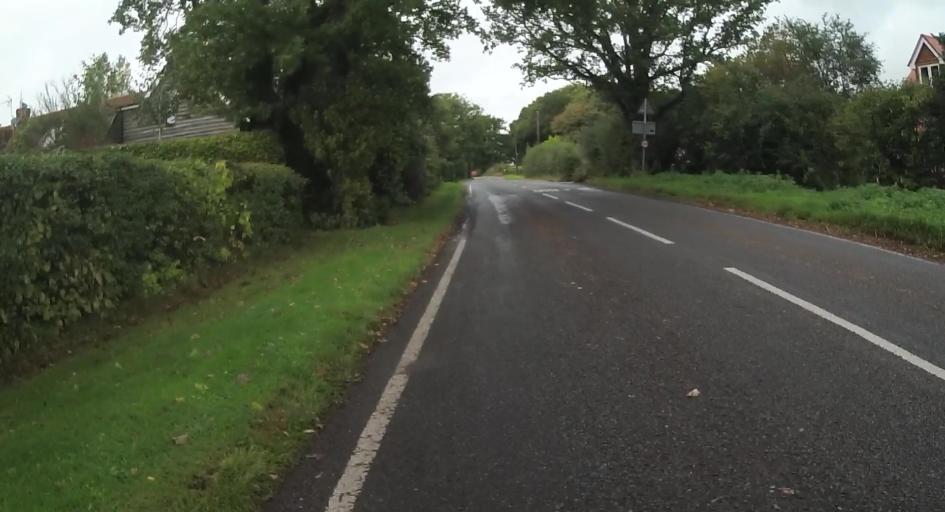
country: GB
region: England
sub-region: Hampshire
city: Tadley
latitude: 51.3449
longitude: -1.1633
